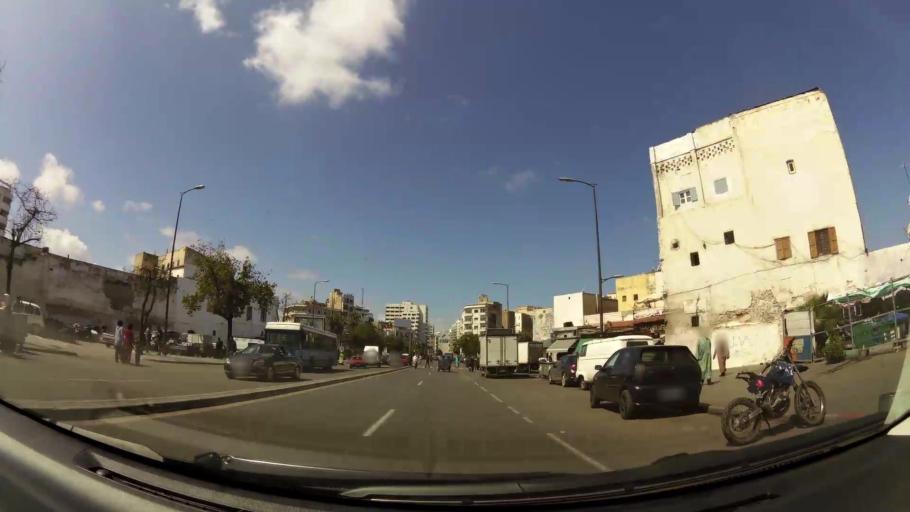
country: MA
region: Grand Casablanca
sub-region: Casablanca
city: Casablanca
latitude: 33.5962
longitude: -7.6226
